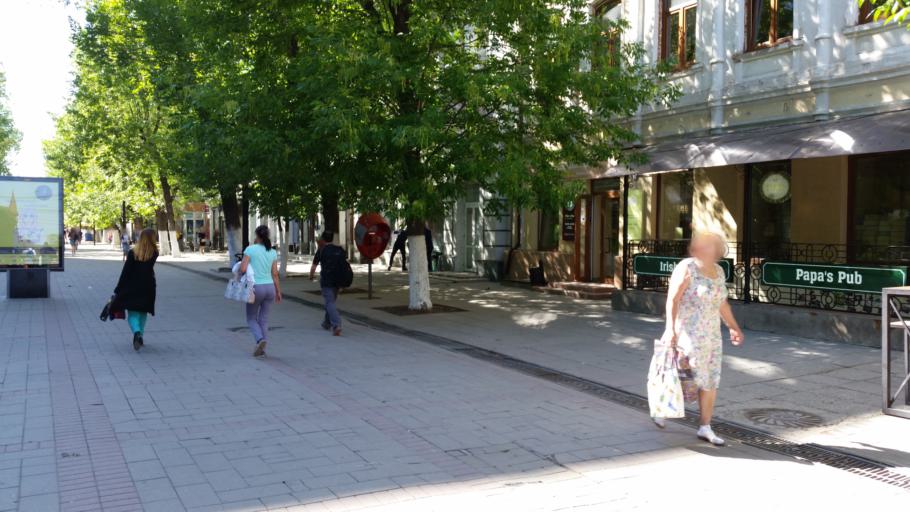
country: RU
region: Saratov
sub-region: Saratovskiy Rayon
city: Saratov
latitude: 51.5311
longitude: 46.0296
